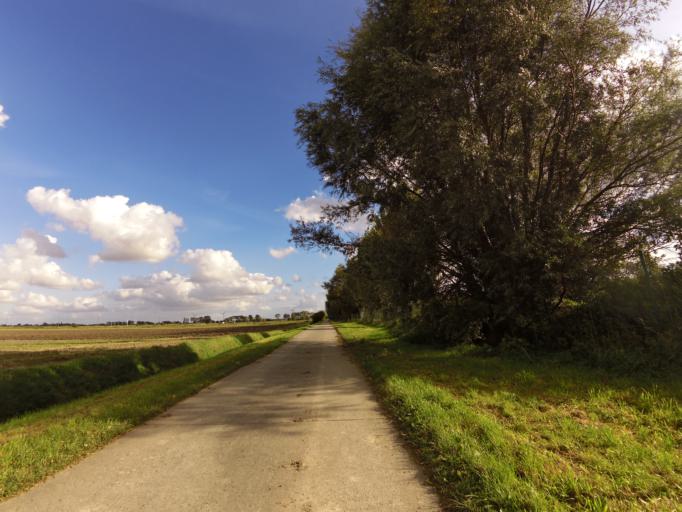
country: BE
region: Flanders
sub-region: Provincie West-Vlaanderen
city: Ostend
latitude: 51.1852
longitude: 2.9347
